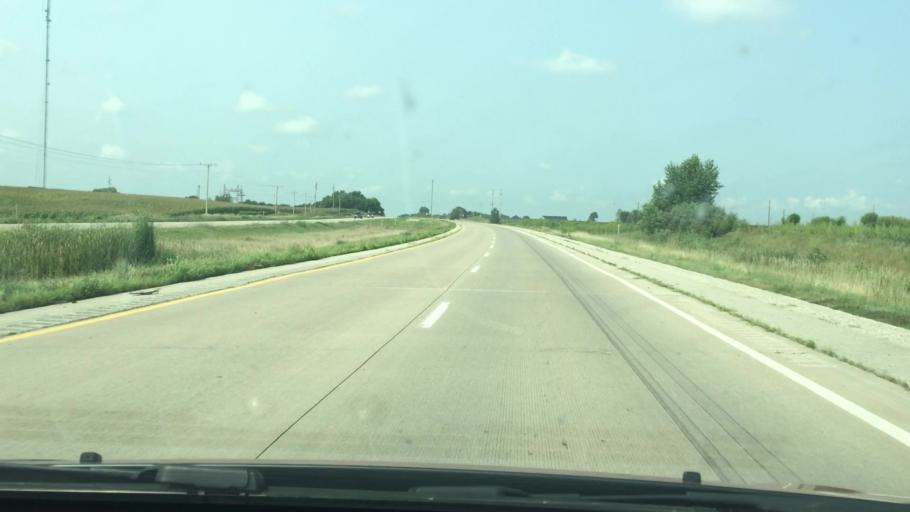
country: US
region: Iowa
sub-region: Cedar County
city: Durant
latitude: 41.5199
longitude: -90.8754
